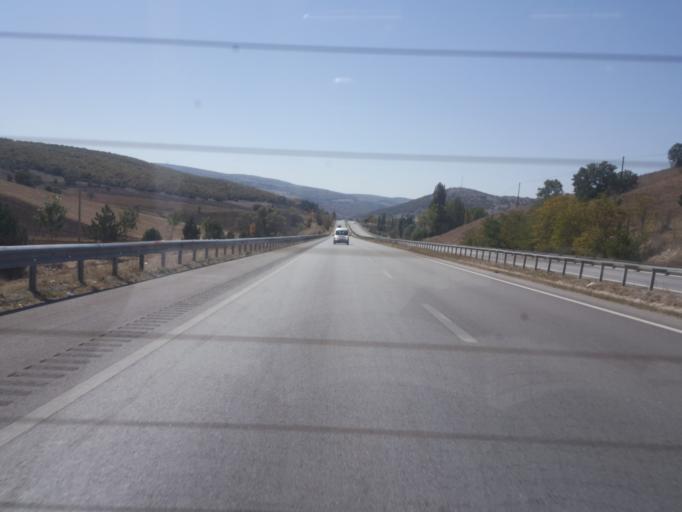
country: TR
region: Corum
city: Alaca
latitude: 40.2862
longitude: 34.6488
